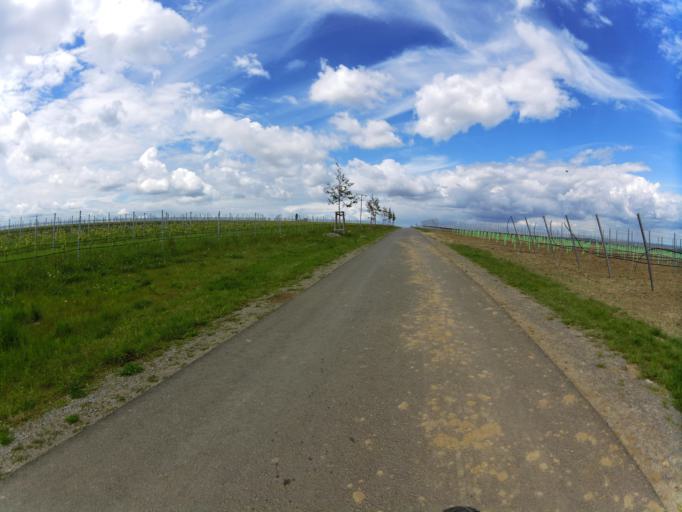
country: DE
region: Bavaria
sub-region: Regierungsbezirk Unterfranken
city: Sommerach
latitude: 49.8397
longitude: 10.1994
